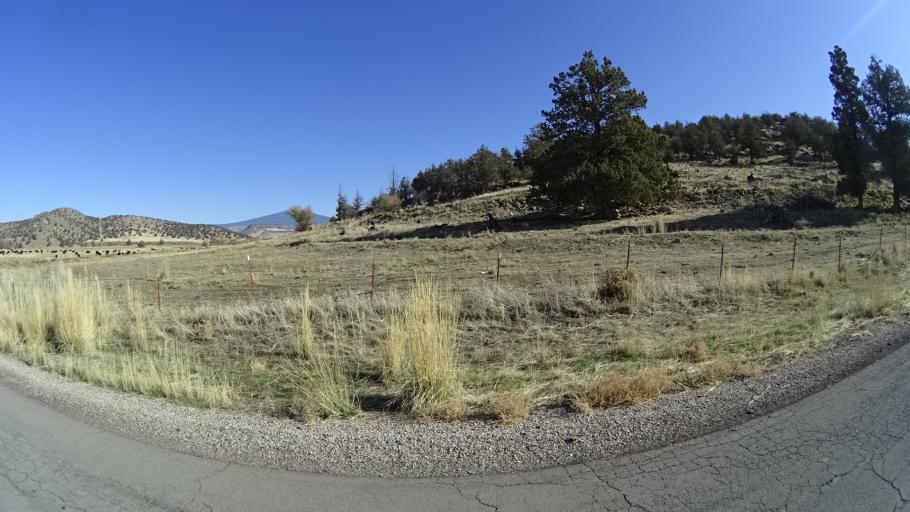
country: US
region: California
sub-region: Siskiyou County
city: Montague
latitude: 41.6925
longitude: -122.3733
